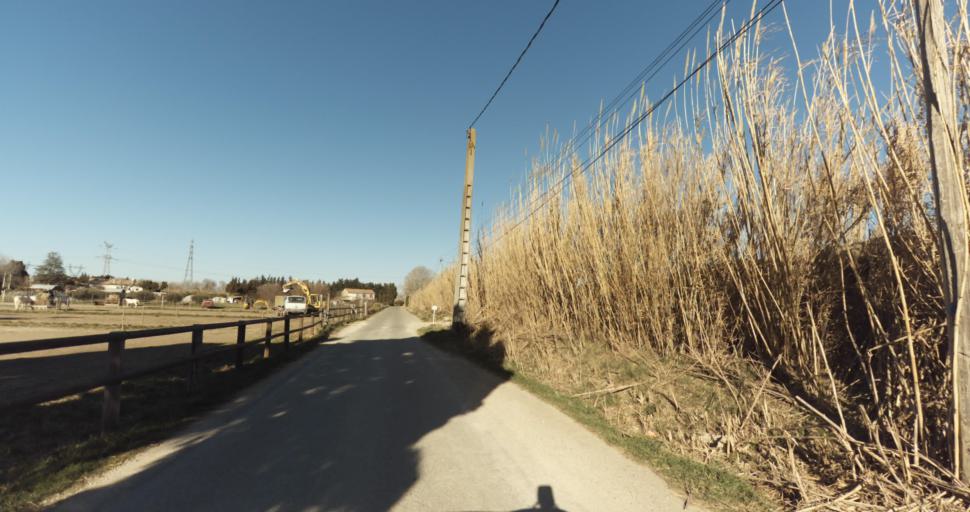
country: FR
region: Provence-Alpes-Cote d'Azur
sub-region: Departement des Bouches-du-Rhone
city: Rognonas
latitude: 43.9098
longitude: 4.7895
